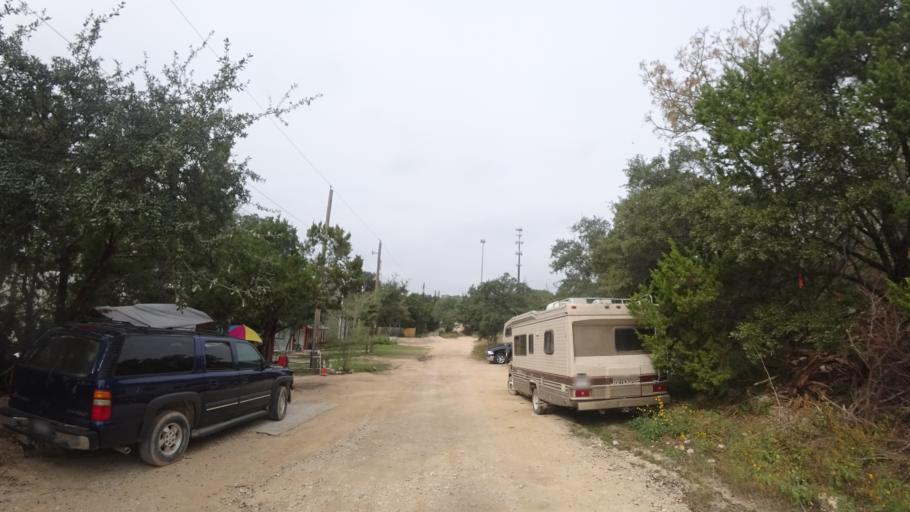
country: US
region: Texas
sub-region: Travis County
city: Hudson Bend
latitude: 30.3956
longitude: -97.9236
